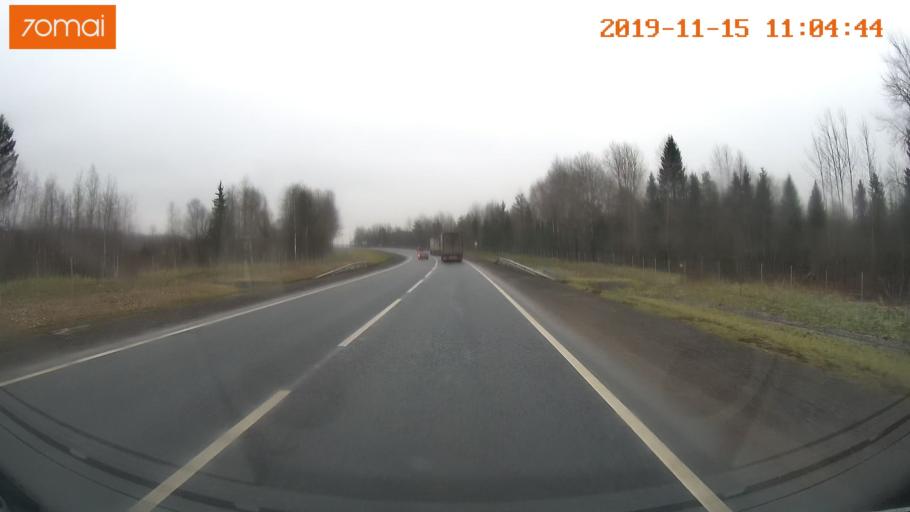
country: RU
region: Vologda
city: Chebsara
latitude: 59.1190
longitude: 38.9890
